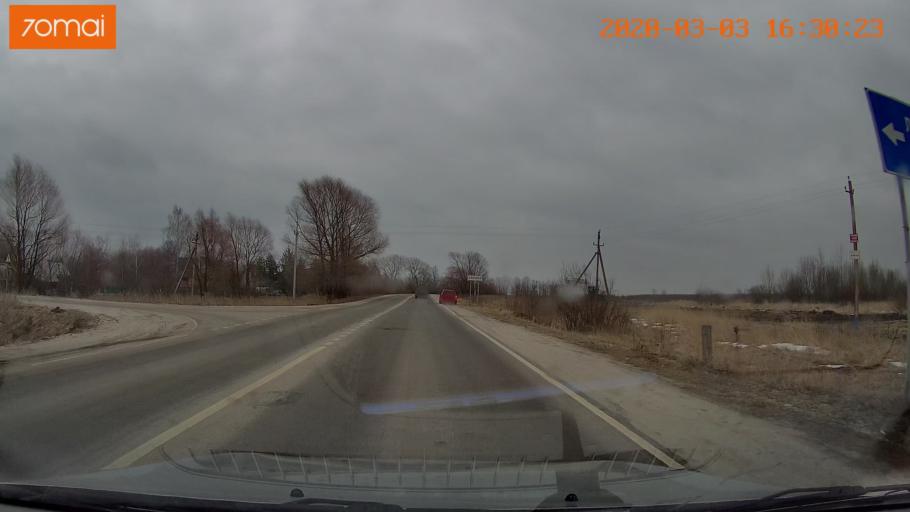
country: RU
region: Moskovskaya
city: Konobeyevo
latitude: 55.4333
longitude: 38.7110
